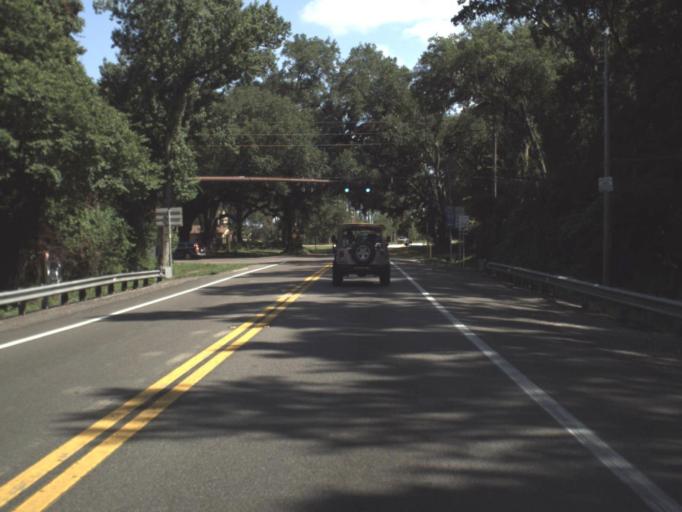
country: US
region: Florida
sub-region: Clay County
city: Green Cove Springs
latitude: 29.9702
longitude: -81.5385
